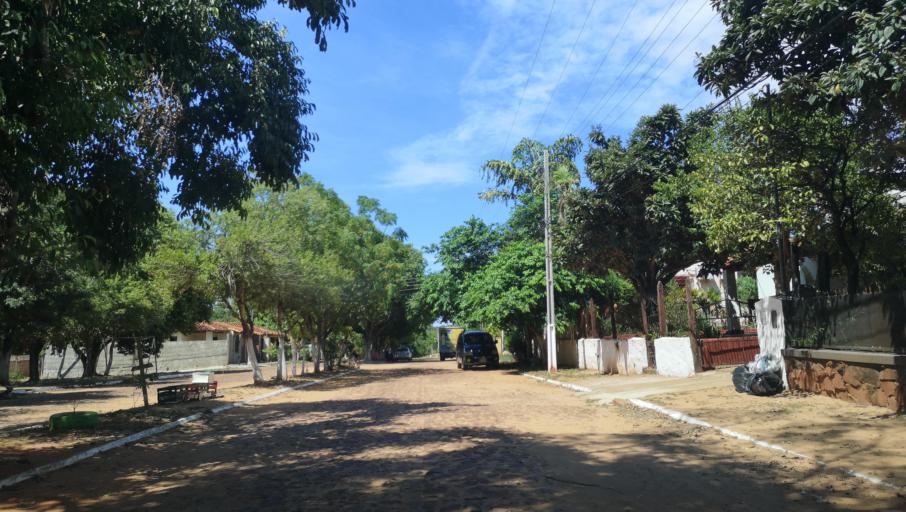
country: PY
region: Misiones
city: Santa Maria
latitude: -26.8795
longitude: -57.0249
